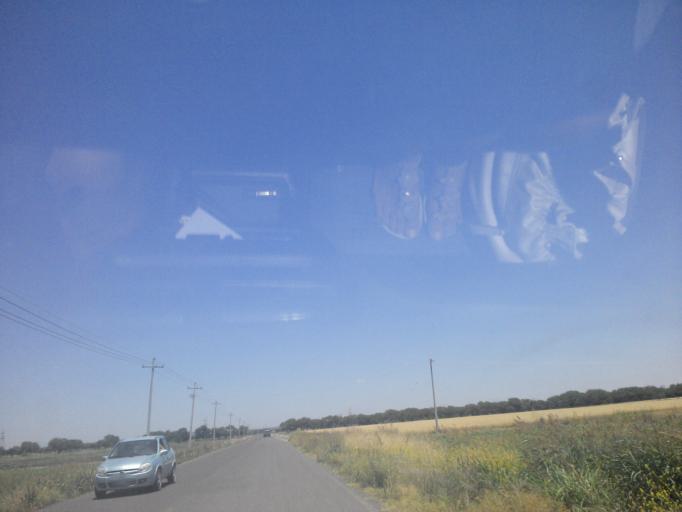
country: MX
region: Guanajuato
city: San Roque
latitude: 20.9545
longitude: -101.8923
